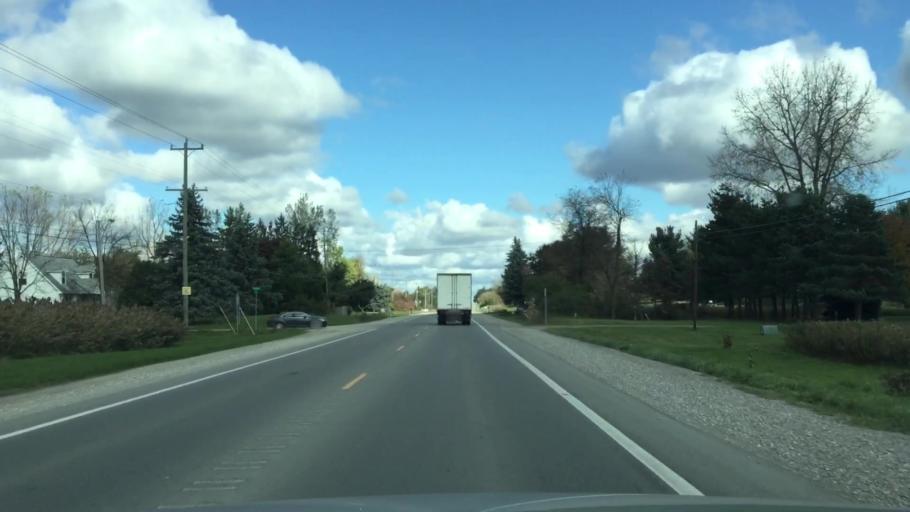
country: US
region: Michigan
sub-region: Oakland County
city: Oxford
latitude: 42.9171
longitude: -83.3126
